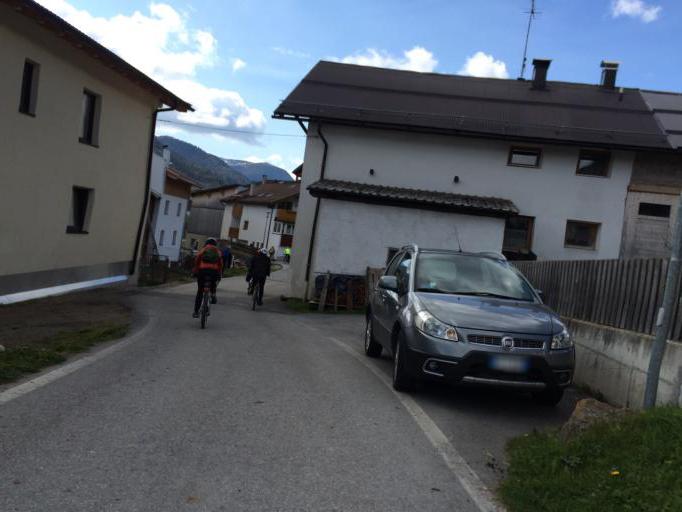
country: IT
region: Trentino-Alto Adige
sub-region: Bolzano
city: Curon Venosta
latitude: 46.7679
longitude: 10.5299
